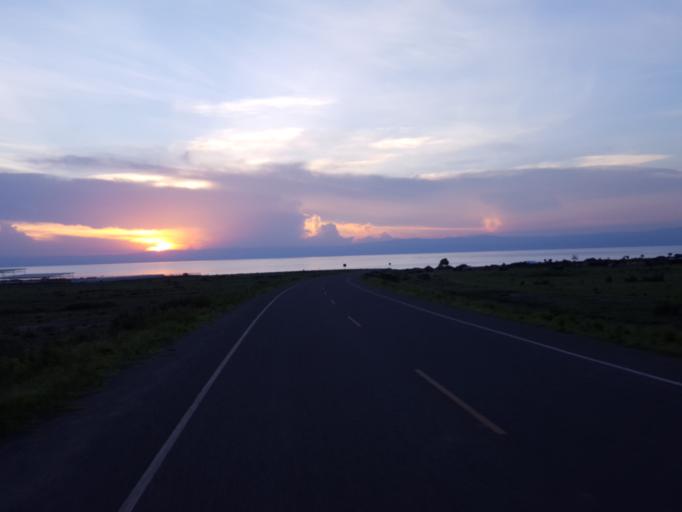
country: UG
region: Western Region
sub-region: Kibale District
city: Kagadi
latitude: 1.2538
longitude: 30.7550
